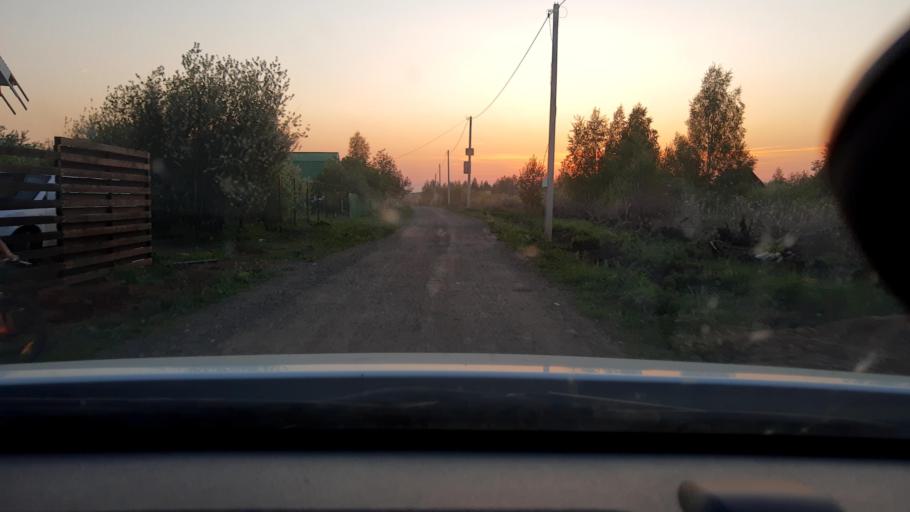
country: RU
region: Bashkortostan
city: Avdon
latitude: 54.5287
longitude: 55.8169
